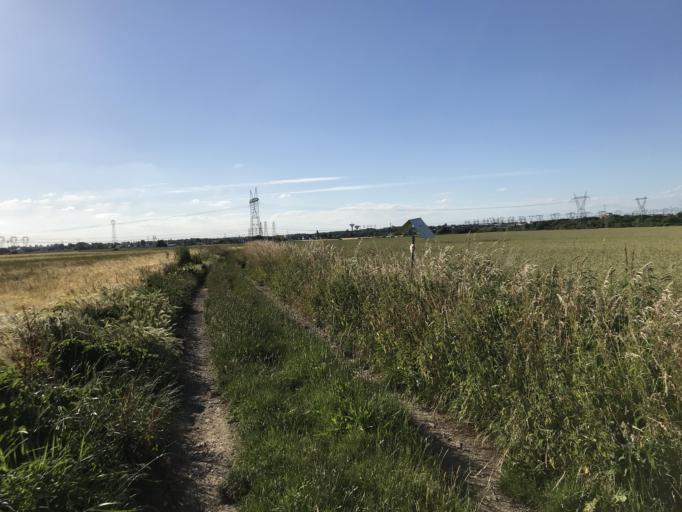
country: FR
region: Ile-de-France
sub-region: Departement de l'Essonne
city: Nozay
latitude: 48.6655
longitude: 2.2326
